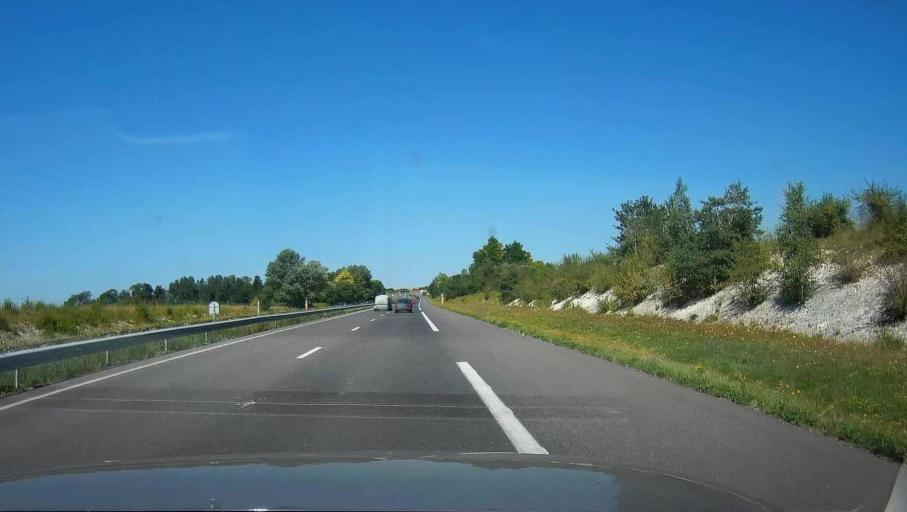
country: FR
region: Champagne-Ardenne
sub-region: Departement de la Marne
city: Fagnieres
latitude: 49.0195
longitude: 4.2916
